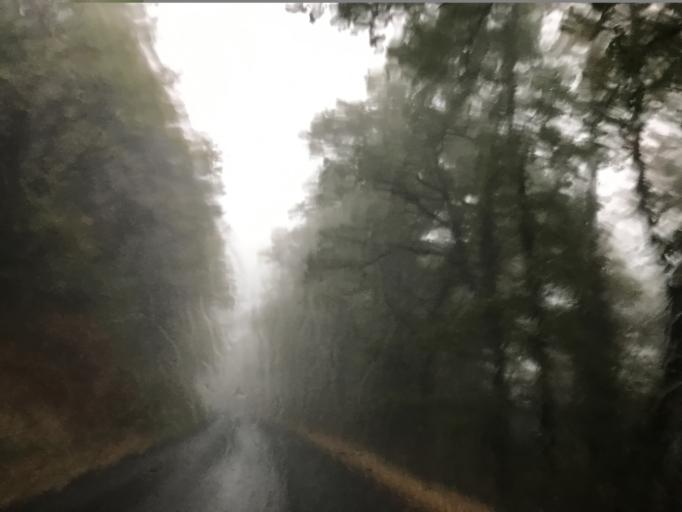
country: FR
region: Auvergne
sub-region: Departement du Puy-de-Dome
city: Escoutoux
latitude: 45.7893
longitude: 3.6145
